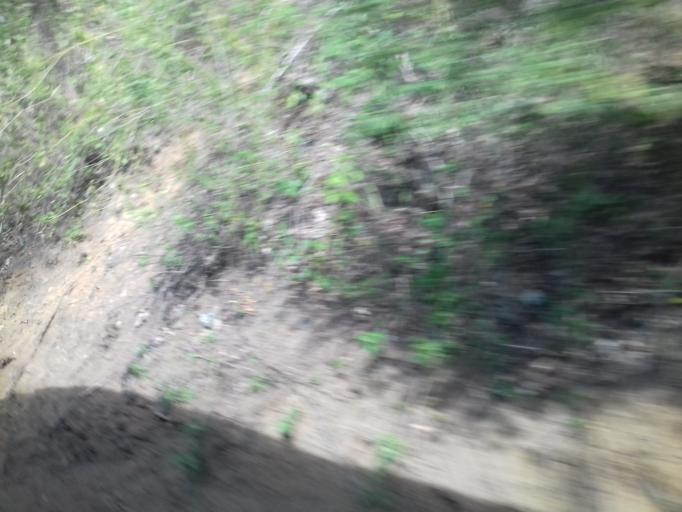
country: CO
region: Antioquia
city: Venecia
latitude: 5.9778
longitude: -75.8279
